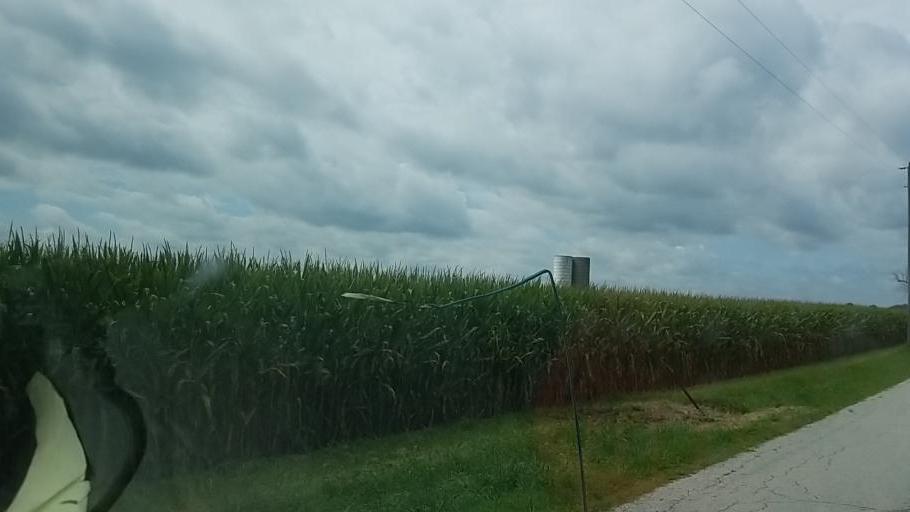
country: US
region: Ohio
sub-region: Fayette County
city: Jeffersonville
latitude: 39.7014
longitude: -83.5768
